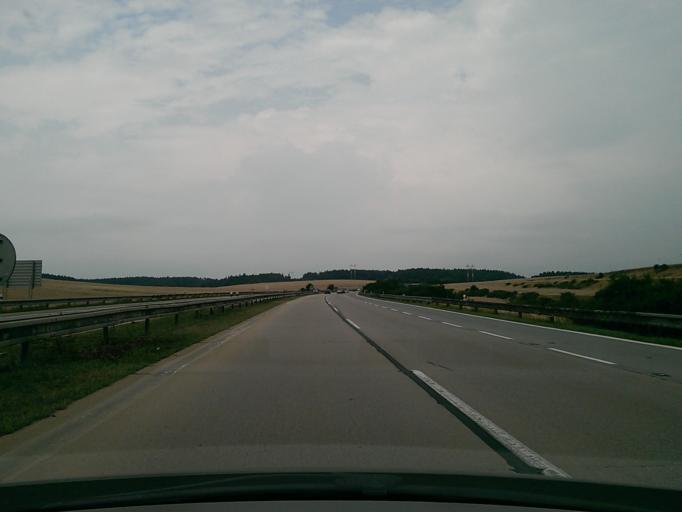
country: CZ
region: South Moravian
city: Ricany
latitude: 49.2214
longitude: 16.3977
